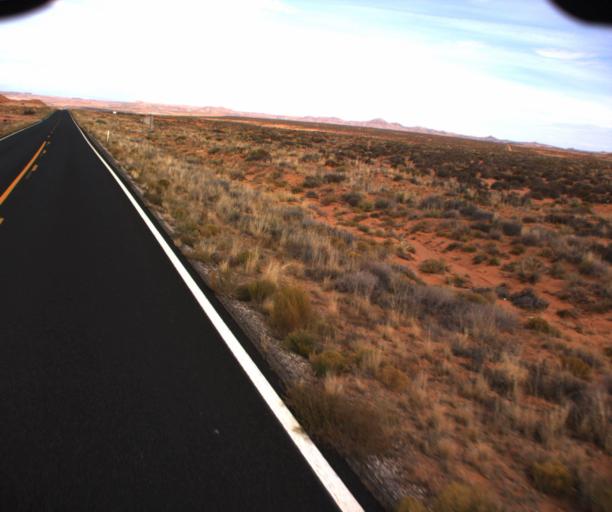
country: US
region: Arizona
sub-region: Apache County
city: Many Farms
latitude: 36.8859
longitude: -109.6278
